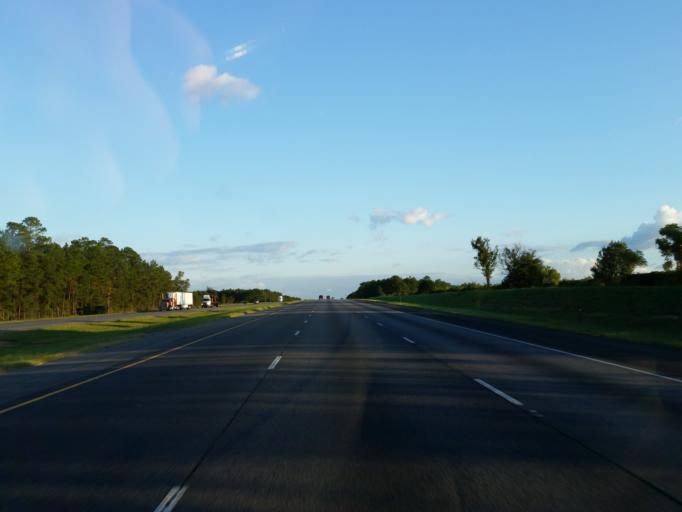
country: US
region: Georgia
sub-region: Crisp County
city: Cordele
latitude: 31.8859
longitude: -83.7299
